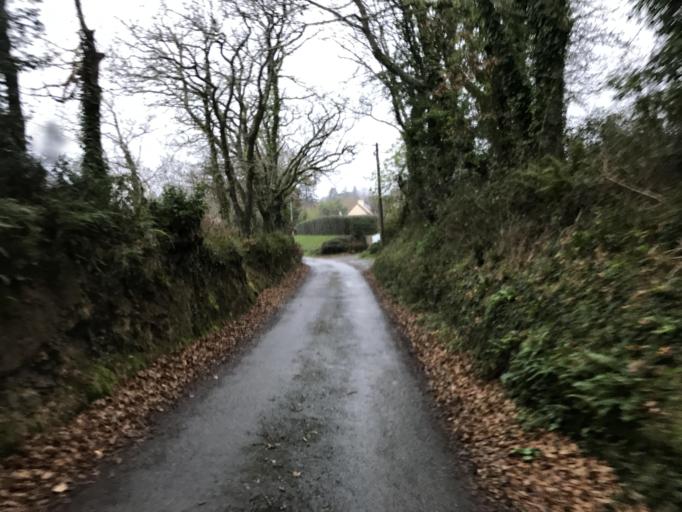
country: FR
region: Brittany
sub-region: Departement du Finistere
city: Logonna-Daoulas
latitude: 48.3235
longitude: -4.2769
